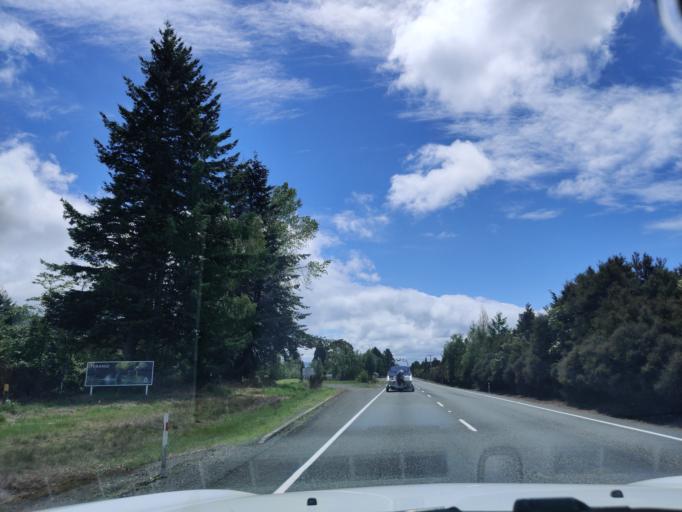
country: NZ
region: Waikato
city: Turangi
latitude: -39.0096
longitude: 175.8065
